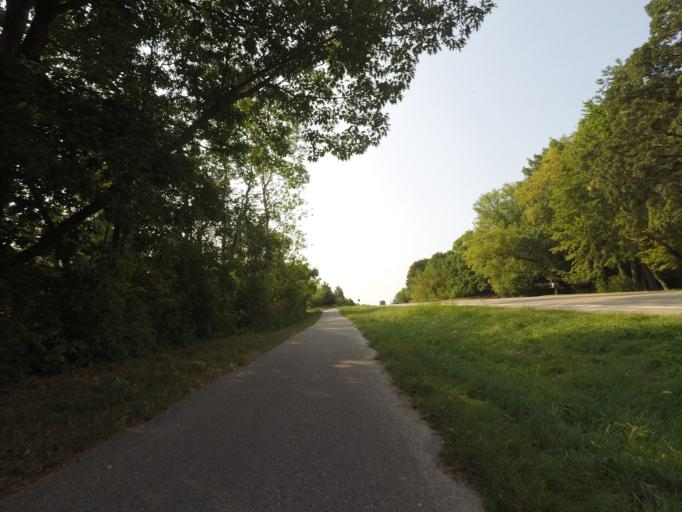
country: US
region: Wisconsin
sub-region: Waukesha County
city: Delafield
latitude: 43.0578
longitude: -88.4140
